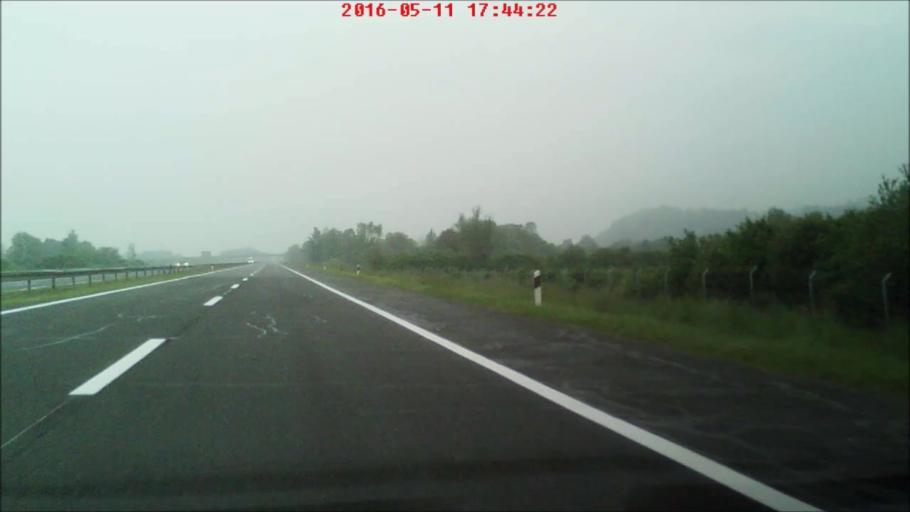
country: HR
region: Zagrebacka
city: Jakovlje
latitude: 45.9861
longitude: 15.8583
